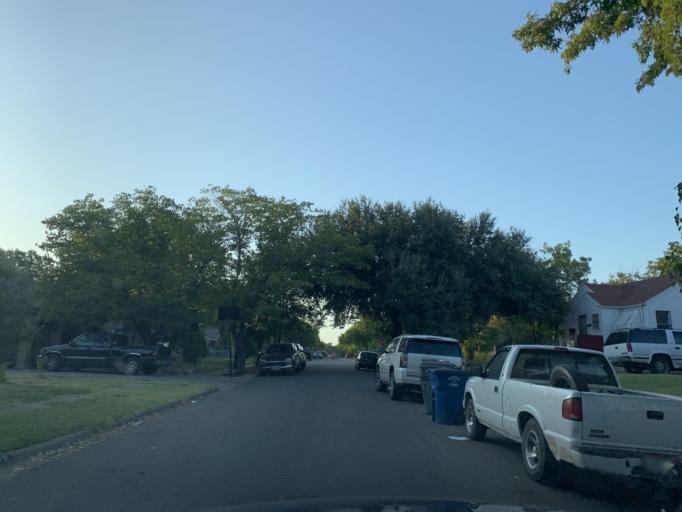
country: US
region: Texas
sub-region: Dallas County
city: Dallas
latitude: 32.7098
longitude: -96.8057
